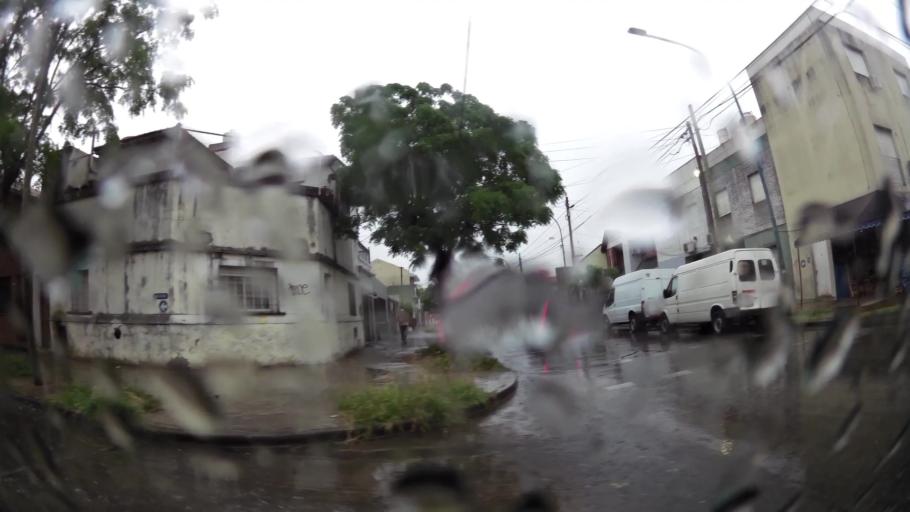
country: AR
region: Buenos Aires
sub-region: Partido de Lanus
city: Lanus
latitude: -34.7107
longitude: -58.3988
